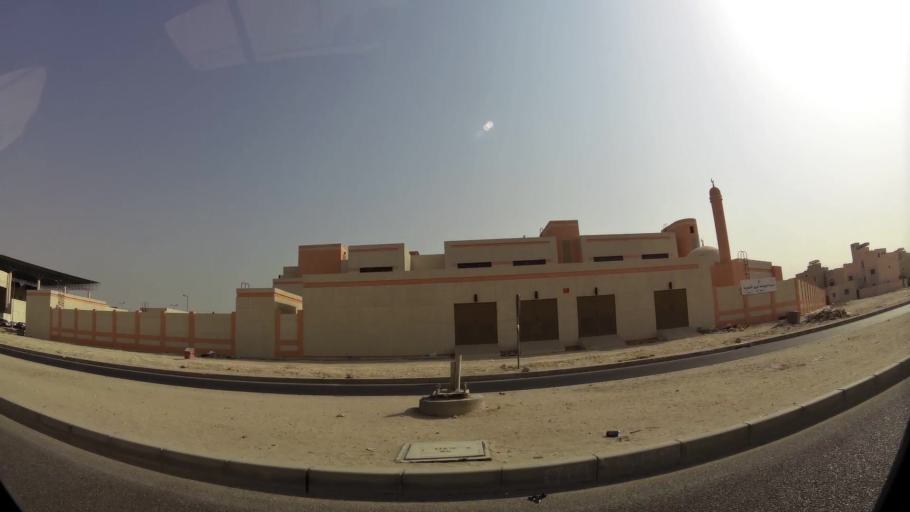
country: KW
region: Muhafazat al Jahra'
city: Al Jahra'
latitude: 29.3580
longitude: 47.7555
